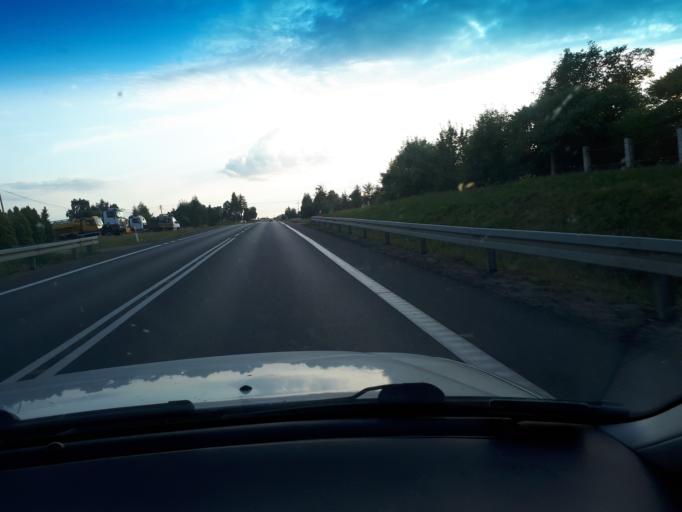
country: PL
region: Subcarpathian Voivodeship
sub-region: Powiat ropczycko-sedziszowski
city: Sedziszow Malopolski
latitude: 50.0673
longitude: 21.6610
